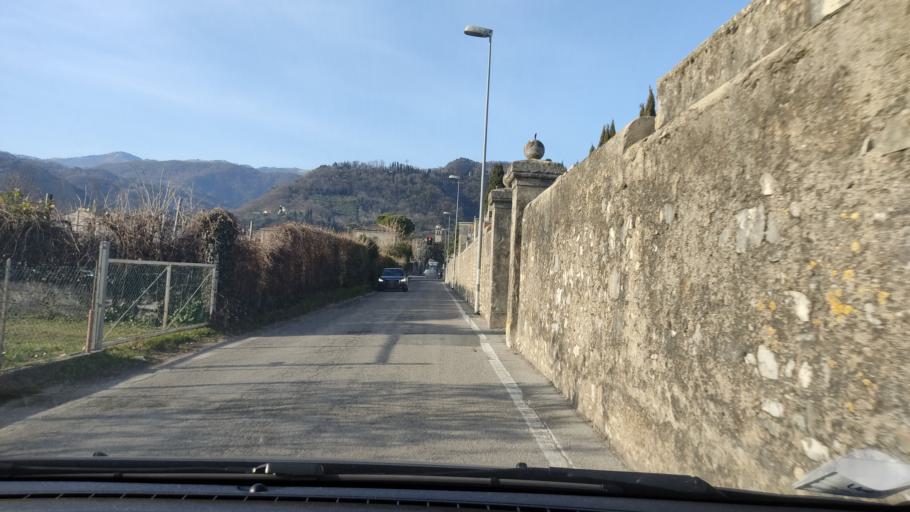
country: IT
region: Veneto
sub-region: Provincia di Treviso
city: Vittorio Veneto
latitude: 45.9703
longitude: 12.2979
